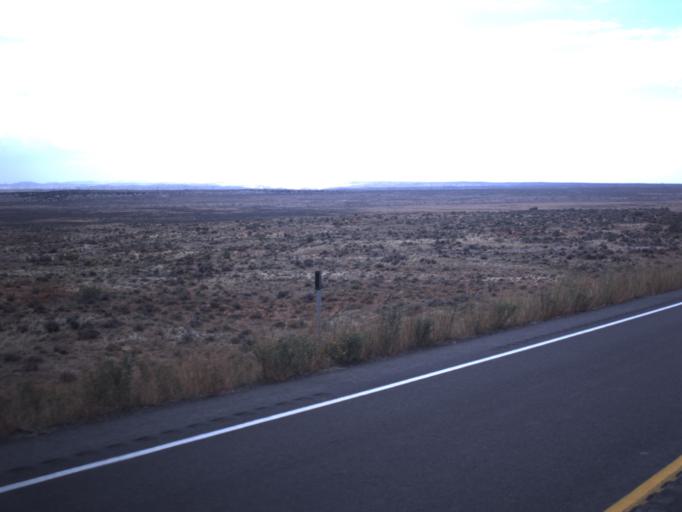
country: US
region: Utah
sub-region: Uintah County
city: Naples
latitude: 40.2550
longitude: -109.4323
